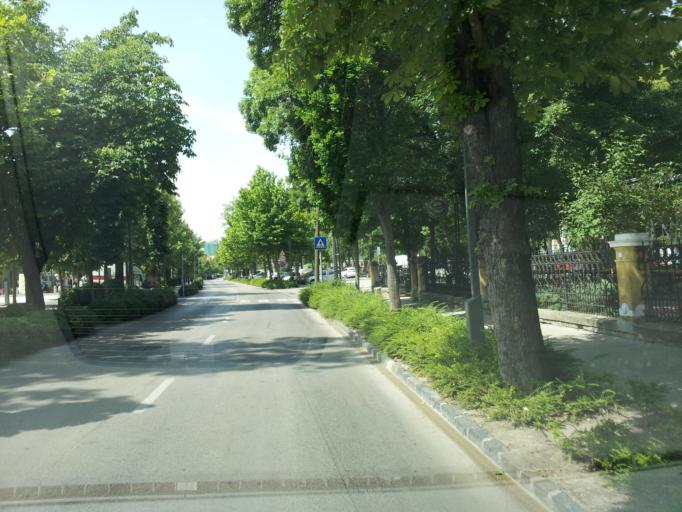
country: HU
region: Veszprem
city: Balatonfured
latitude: 46.9535
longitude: 17.8921
